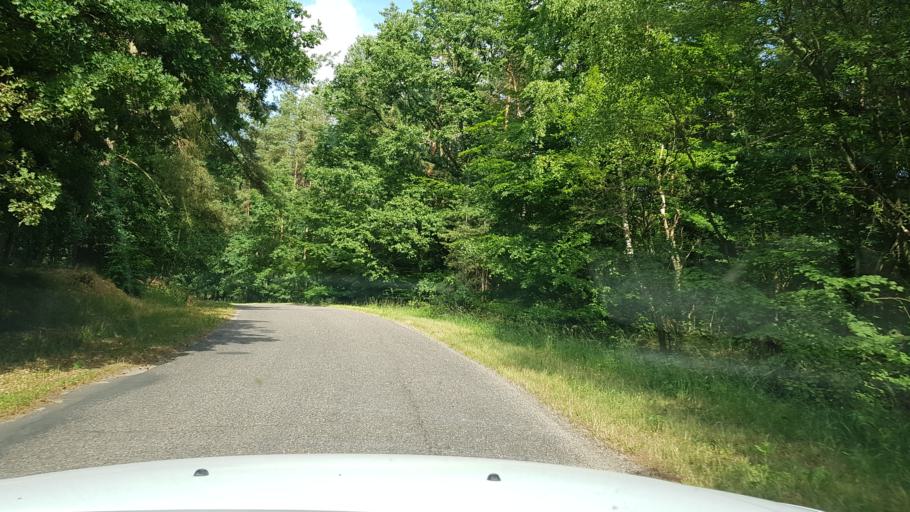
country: PL
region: West Pomeranian Voivodeship
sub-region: Powiat goleniowski
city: Mosty
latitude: 53.5545
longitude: 14.9725
